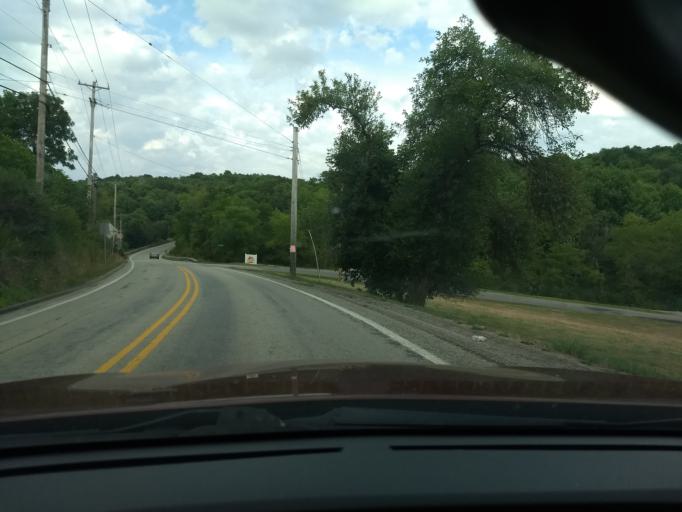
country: US
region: Pennsylvania
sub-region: Allegheny County
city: Bakerstown
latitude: 40.6544
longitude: -79.8929
